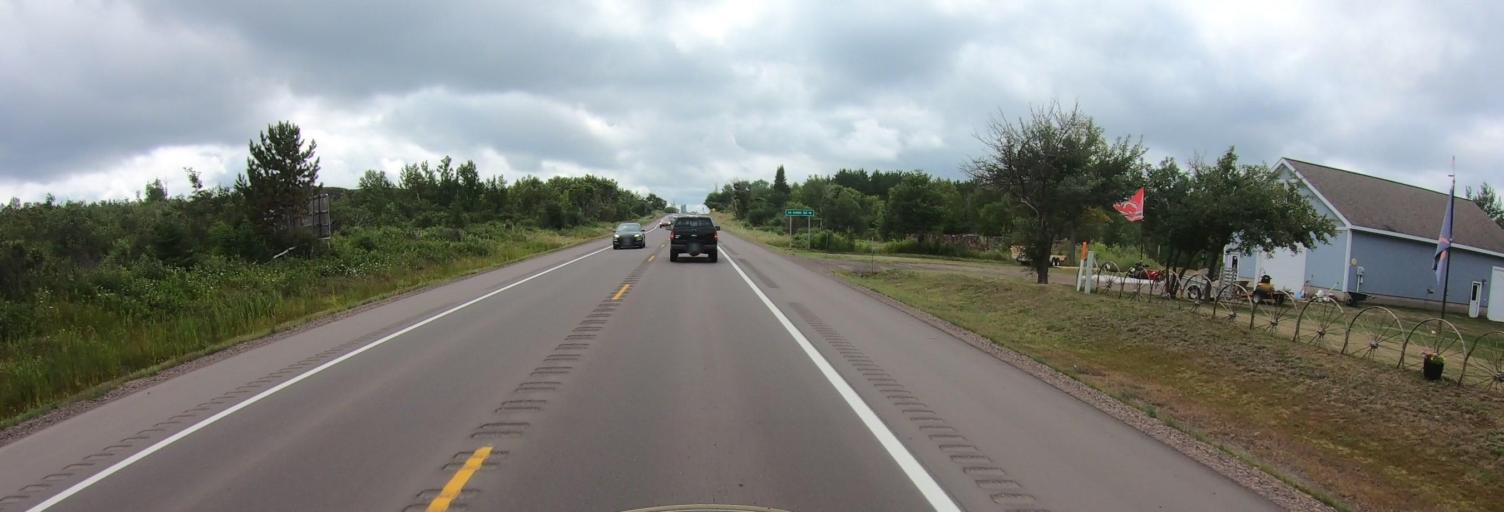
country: US
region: Michigan
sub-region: Houghton County
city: Hancock
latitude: 47.1474
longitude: -88.5663
